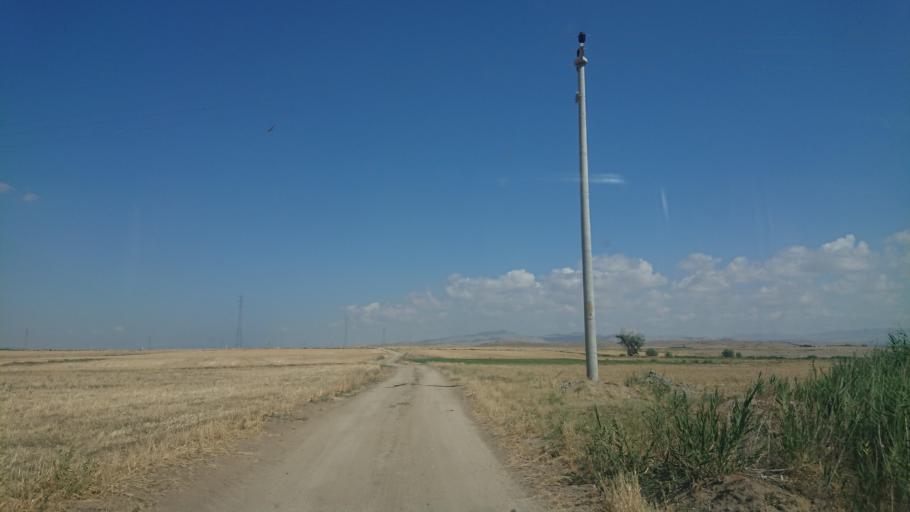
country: TR
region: Aksaray
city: Sariyahsi
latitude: 38.9977
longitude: 33.8937
